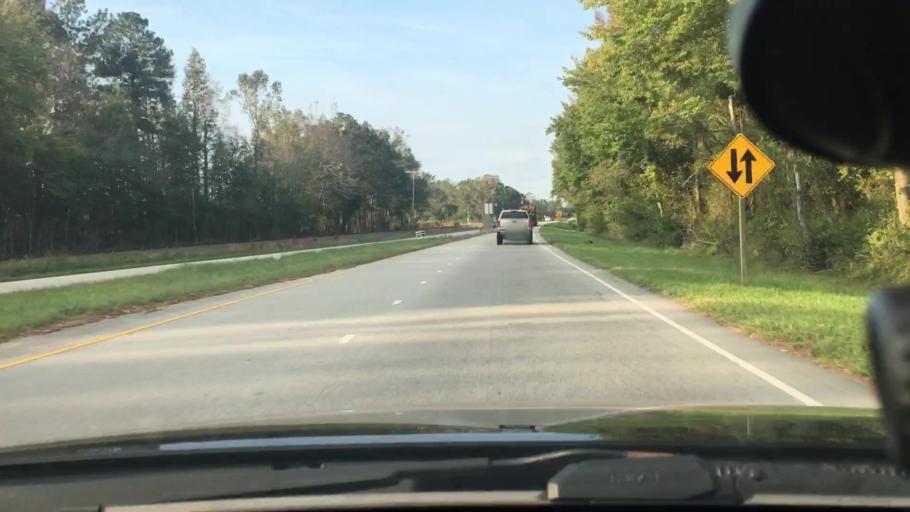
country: US
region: North Carolina
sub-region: Craven County
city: Vanceboro
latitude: 35.3358
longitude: -77.1511
